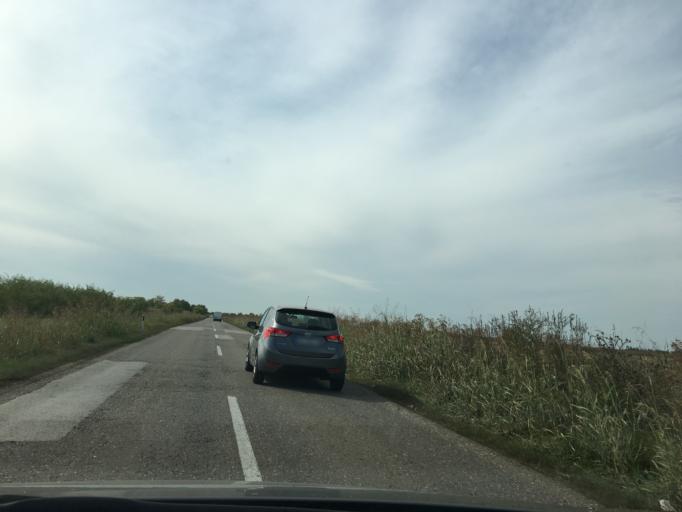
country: RS
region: Autonomna Pokrajina Vojvodina
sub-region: Juznobacki Okrug
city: Temerin
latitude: 45.4763
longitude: 19.9227
